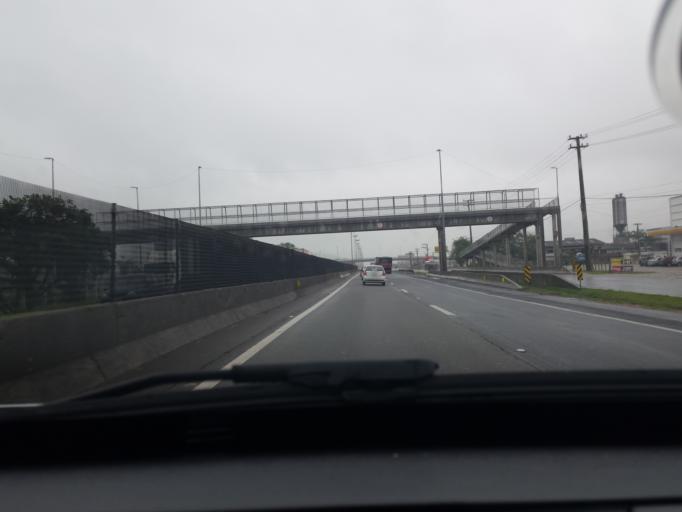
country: BR
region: Santa Catarina
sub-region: Itajai
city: Itajai
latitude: -26.9229
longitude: -48.7077
